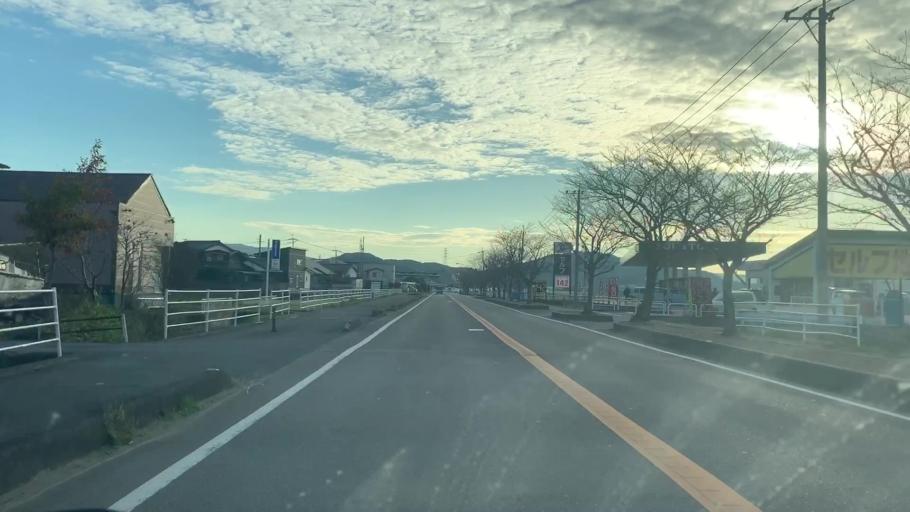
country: JP
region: Saga Prefecture
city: Karatsu
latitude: 33.4125
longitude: 129.9930
